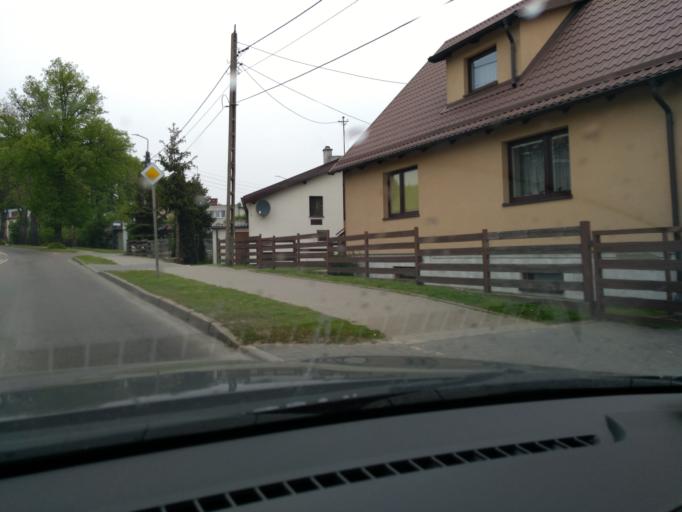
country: PL
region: Pomeranian Voivodeship
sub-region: Powiat kartuski
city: Kartuzy
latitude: 54.3372
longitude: 18.1878
